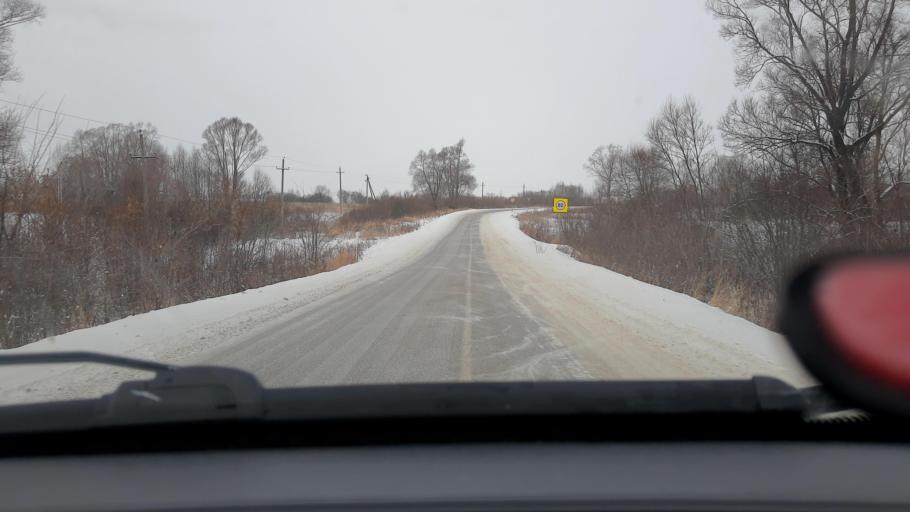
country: RU
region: Bashkortostan
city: Iglino
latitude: 54.6812
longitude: 56.4158
